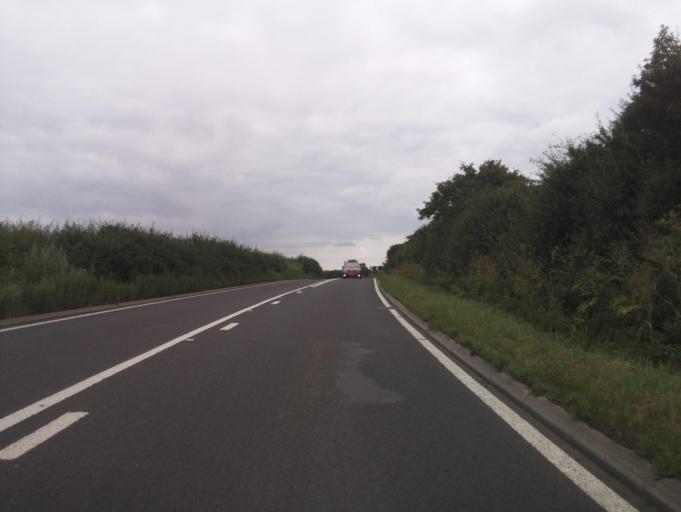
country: GB
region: England
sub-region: Lincolnshire
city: Barrowby
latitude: 52.9334
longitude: -0.7479
